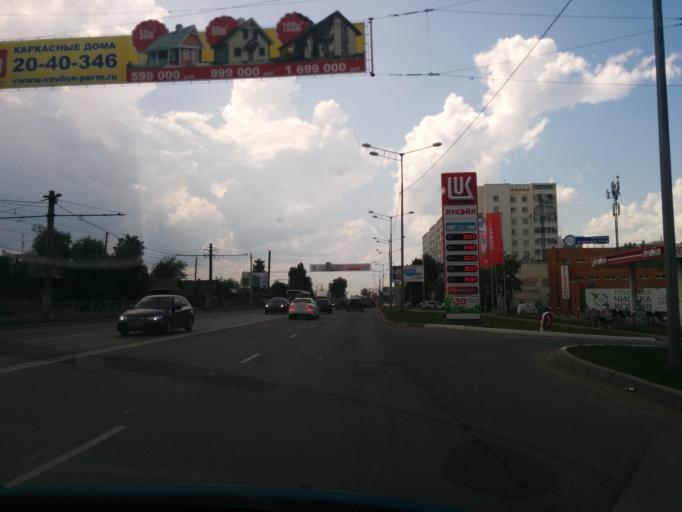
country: RU
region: Perm
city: Kondratovo
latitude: 57.9680
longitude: 56.1493
